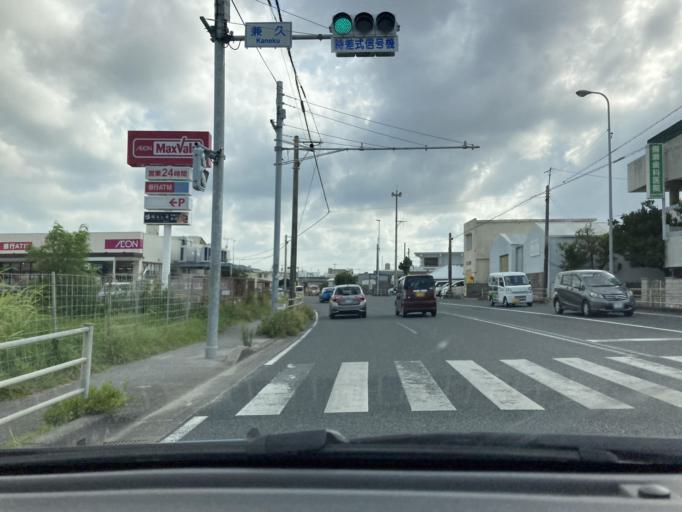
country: JP
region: Okinawa
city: Ginowan
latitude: 26.2178
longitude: 127.7641
